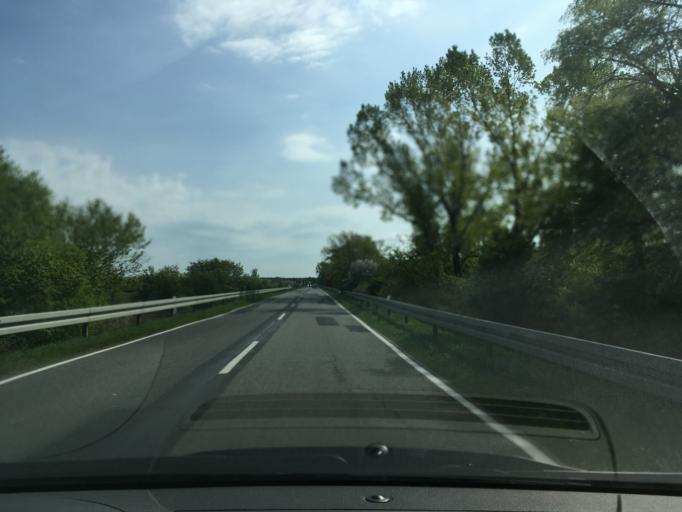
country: PL
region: Lublin Voivodeship
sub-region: Powiat rycki
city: Deblin
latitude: 51.4759
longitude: 21.8929
